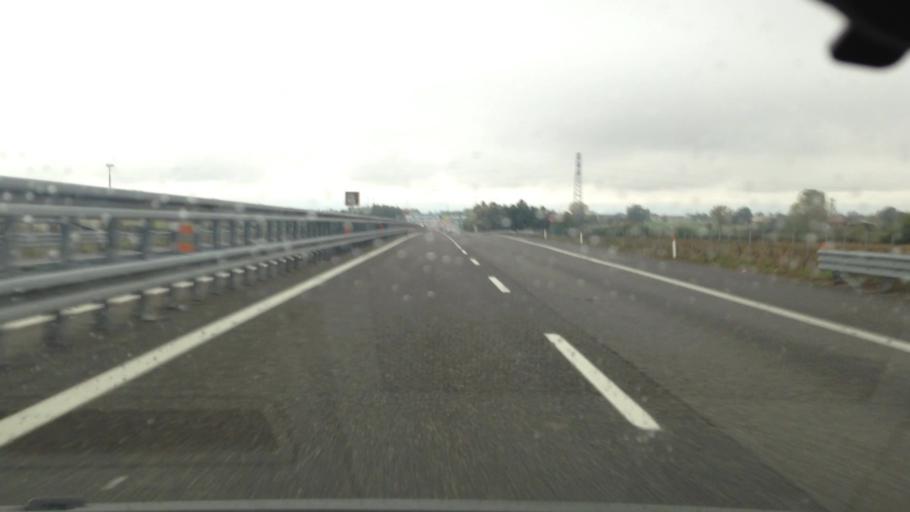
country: IT
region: Piedmont
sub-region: Provincia di Asti
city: Villanova d'Asti
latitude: 44.9514
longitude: 7.9374
